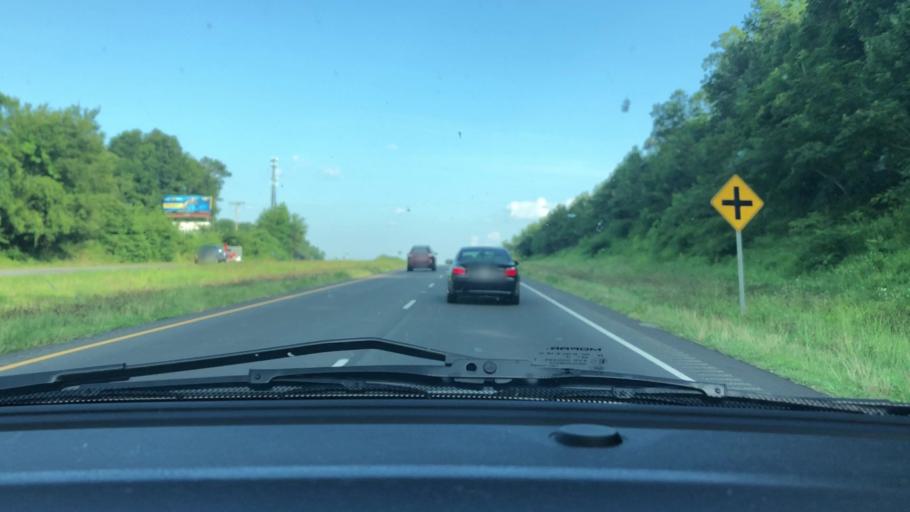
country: US
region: North Carolina
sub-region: Chatham County
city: Siler City
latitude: 35.6549
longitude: -79.3951
